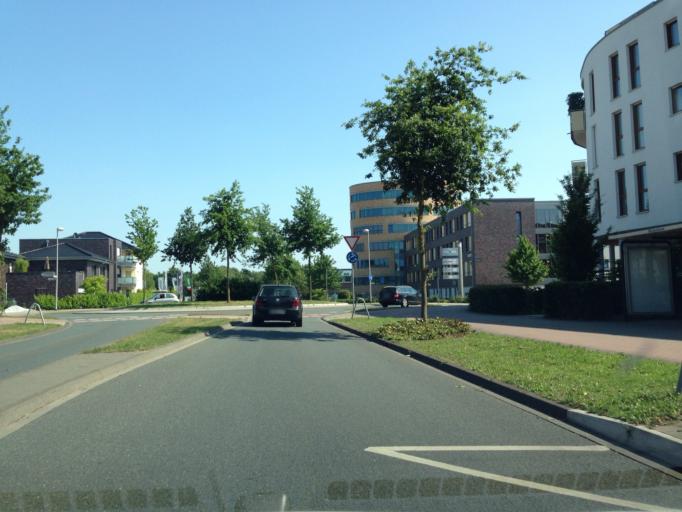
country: DE
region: North Rhine-Westphalia
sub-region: Regierungsbezirk Munster
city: Muenster
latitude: 51.9596
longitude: 7.5697
